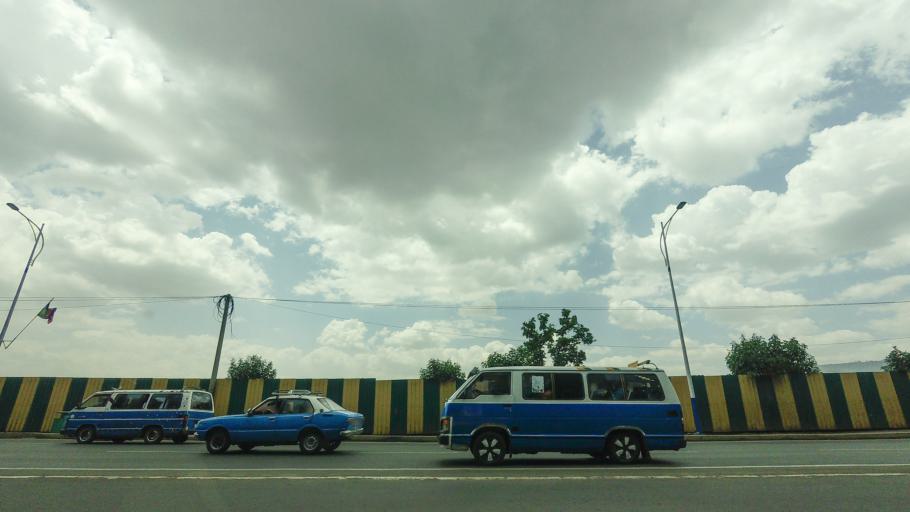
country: ET
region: Adis Abeba
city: Addis Ababa
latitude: 9.0254
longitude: 38.7617
